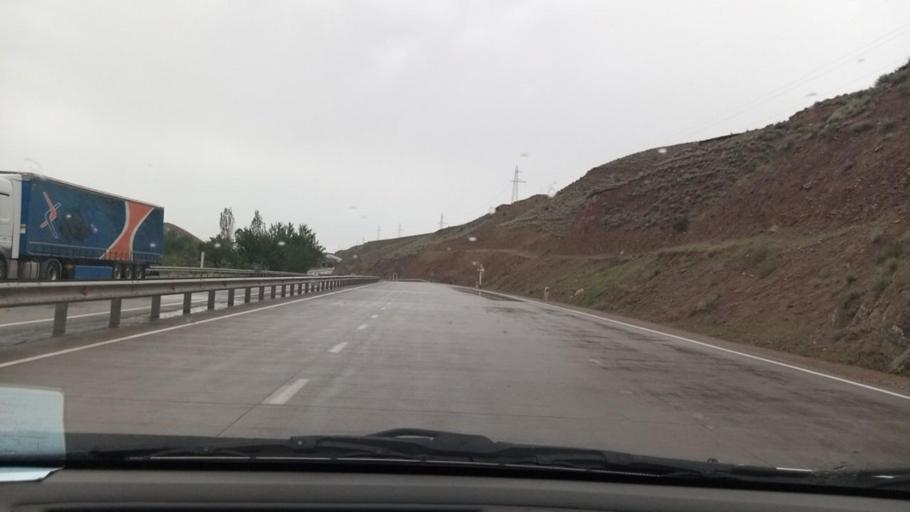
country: TJ
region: Viloyati Sughd
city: Shaydon
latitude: 40.9528
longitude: 70.6753
